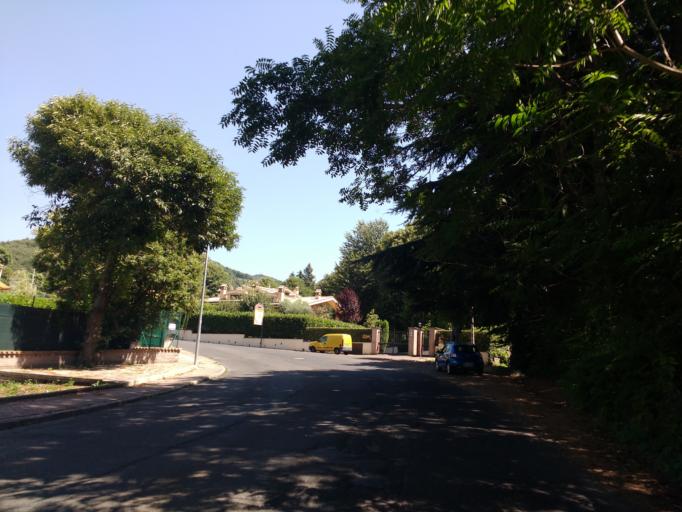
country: IT
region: Latium
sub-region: Citta metropolitana di Roma Capitale
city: Rocca di Papa
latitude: 41.7695
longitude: 12.7079
